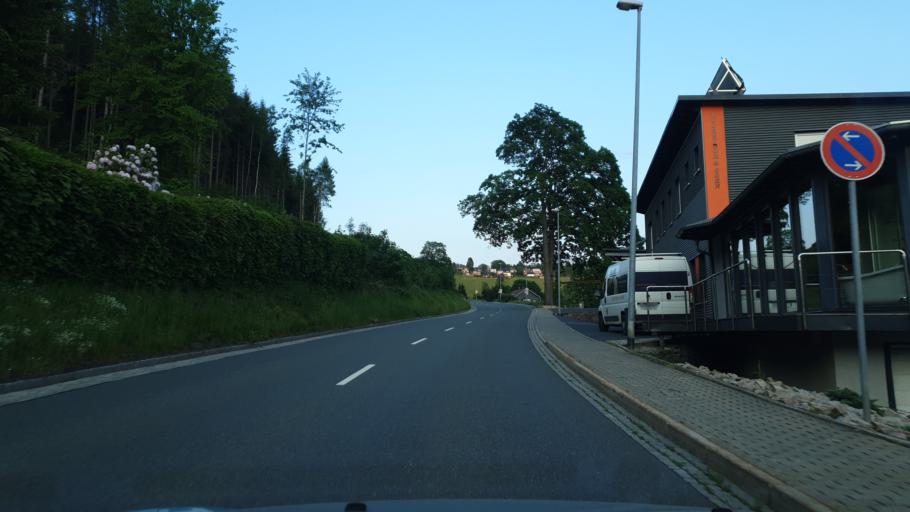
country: DE
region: Saxony
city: Klingenthal
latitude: 50.3857
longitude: 12.4847
